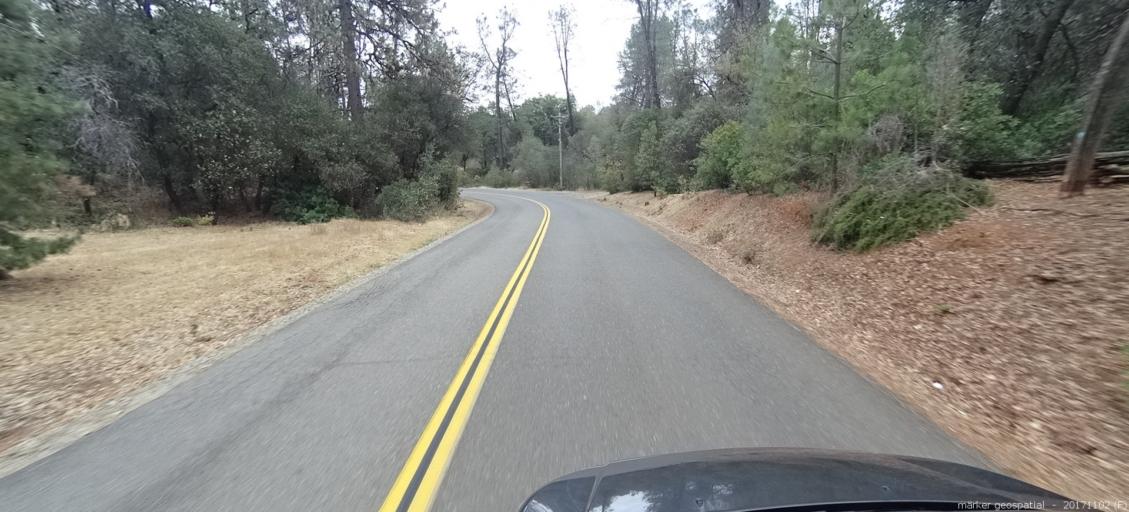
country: US
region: California
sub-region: Shasta County
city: Central Valley (historical)
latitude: 40.6631
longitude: -122.4016
